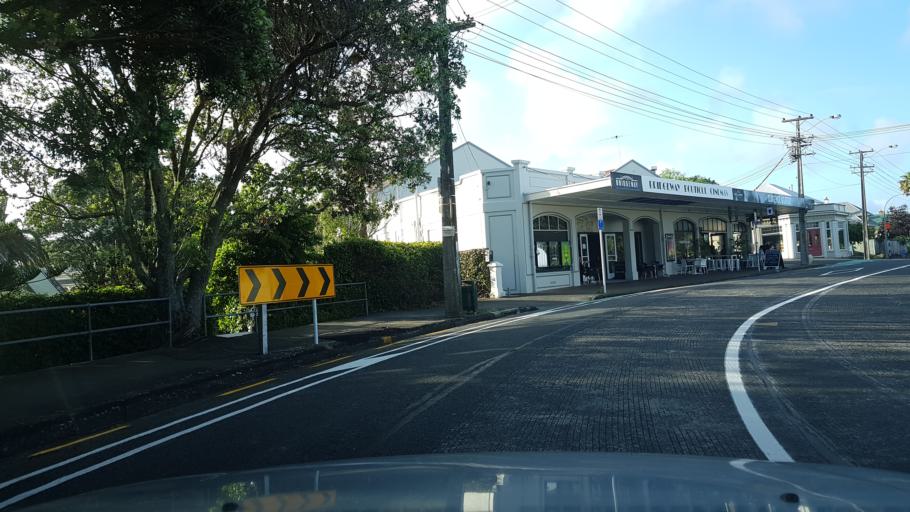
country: NZ
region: Auckland
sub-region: Auckland
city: North Shore
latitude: -36.8184
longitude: 174.7453
